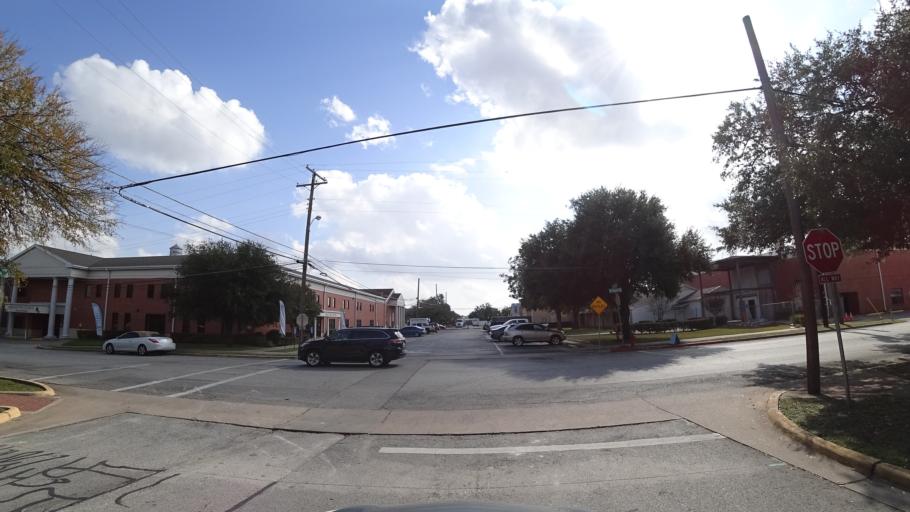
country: US
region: Texas
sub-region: Williamson County
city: Round Rock
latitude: 30.5099
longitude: -97.6817
